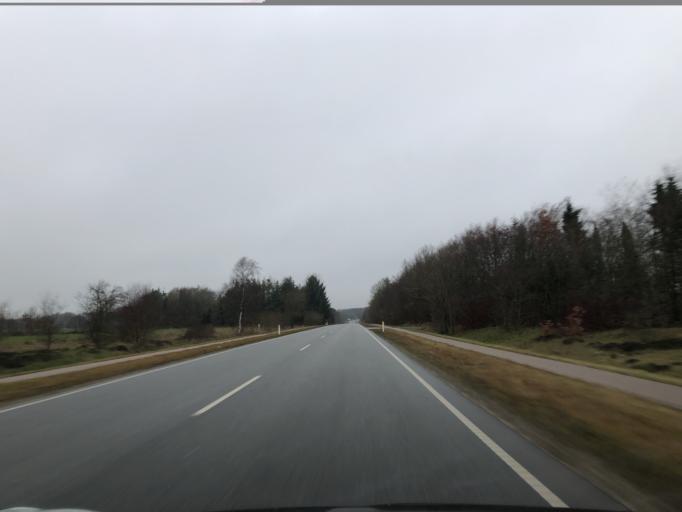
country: DK
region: Central Jutland
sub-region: Herning Kommune
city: Lind
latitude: 56.0754
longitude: 8.9864
